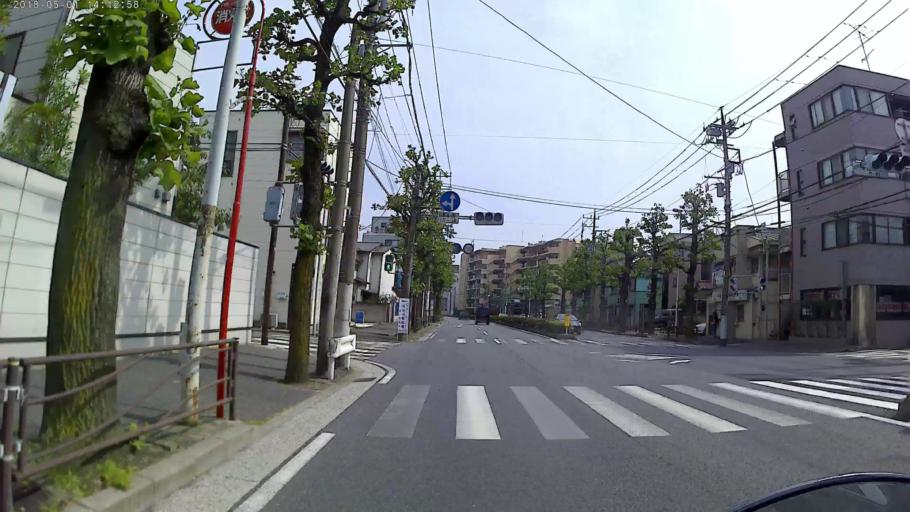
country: JP
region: Kanagawa
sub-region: Kawasaki-shi
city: Kawasaki
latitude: 35.5666
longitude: 139.6707
